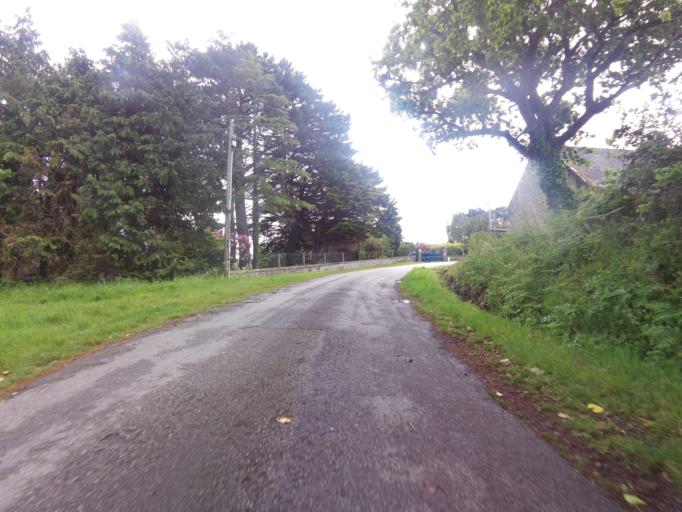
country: FR
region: Brittany
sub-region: Departement du Morbihan
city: Baden
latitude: 47.5994
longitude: -2.9360
